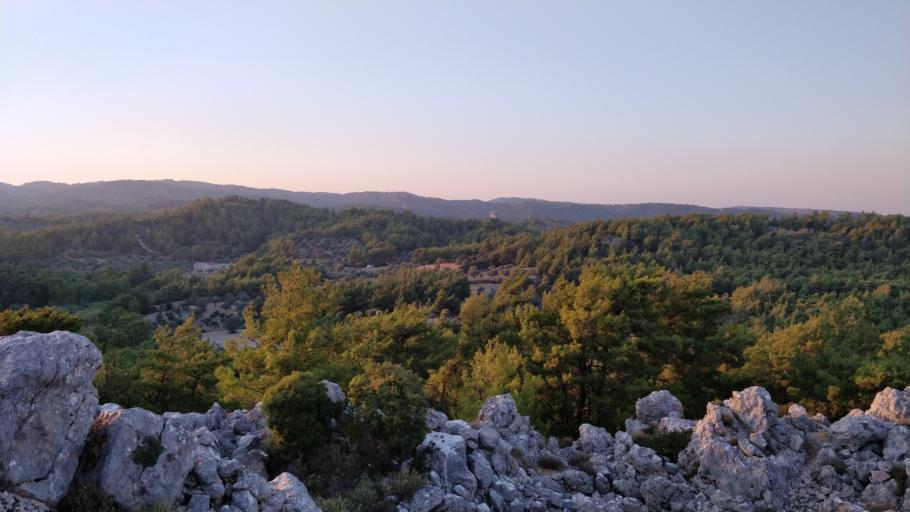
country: GR
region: South Aegean
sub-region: Nomos Dodekanisou
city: Archangelos
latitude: 36.2641
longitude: 28.0759
